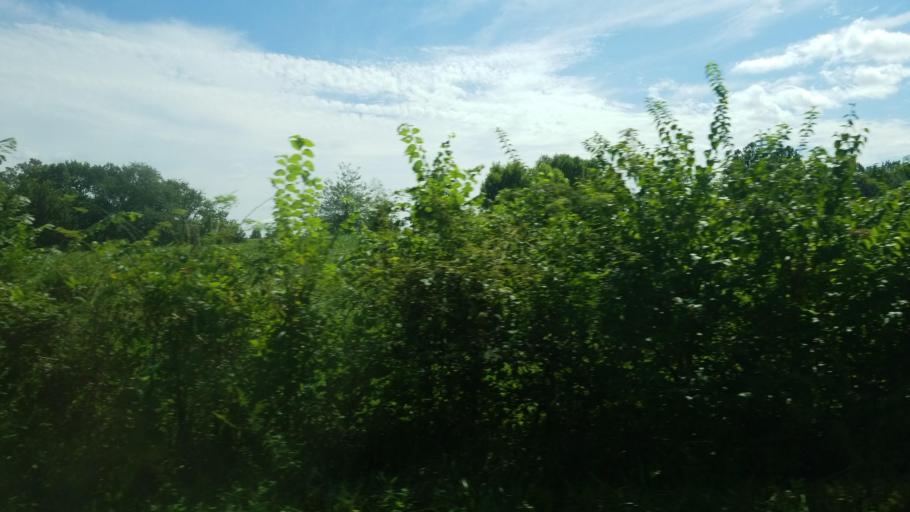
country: US
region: Illinois
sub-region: Williamson County
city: Johnston City
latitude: 37.7902
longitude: -88.8195
